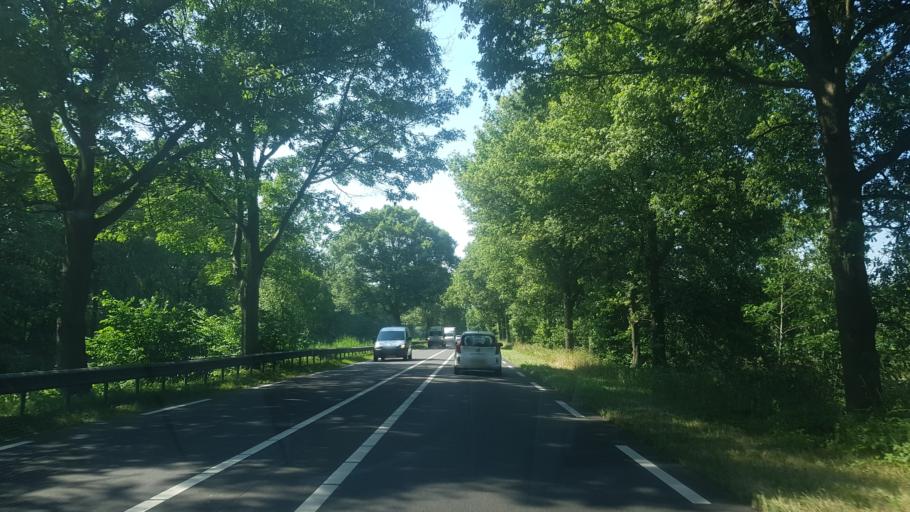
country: NL
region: North Brabant
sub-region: Gemeente Veghel
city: Keldonk
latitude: 51.5627
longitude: 5.6039
